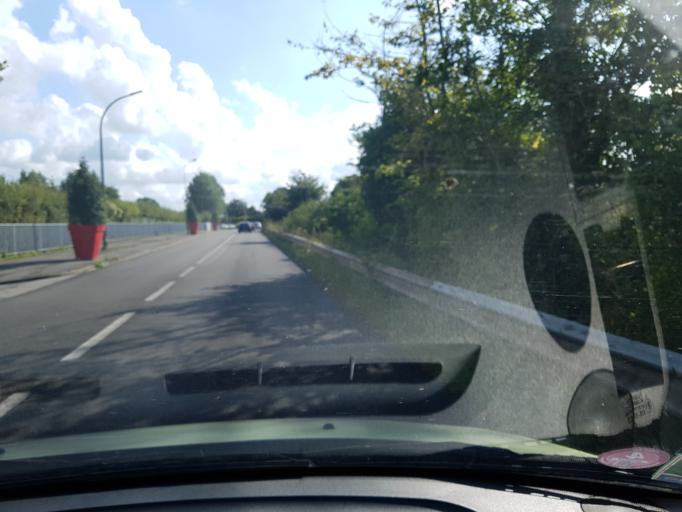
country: FR
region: Nord-Pas-de-Calais
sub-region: Departement du Nord
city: Coudekerque-Branche
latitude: 51.0224
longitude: 2.3976
